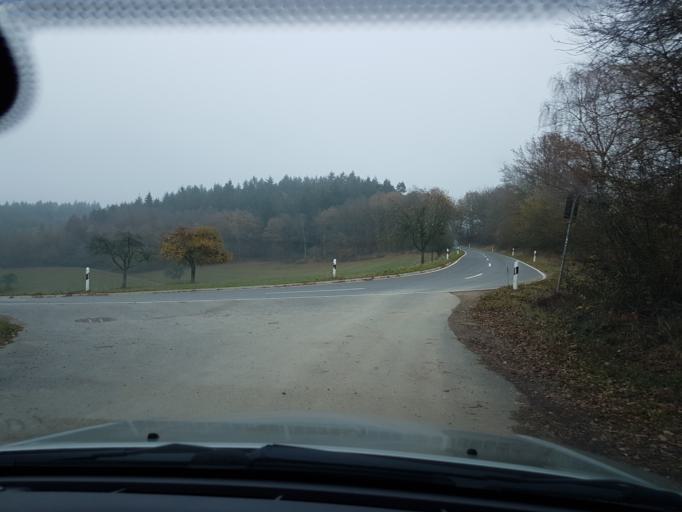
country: DE
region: Hesse
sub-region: Regierungsbezirk Darmstadt
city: Bad Schwalbach
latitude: 50.0957
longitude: 8.0250
